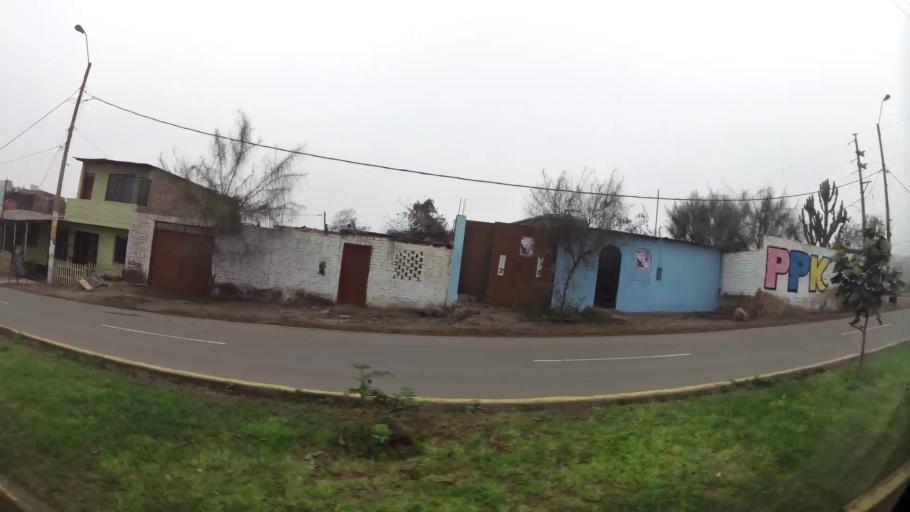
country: PE
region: Lima
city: Ventanilla
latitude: -11.8341
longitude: -77.1081
